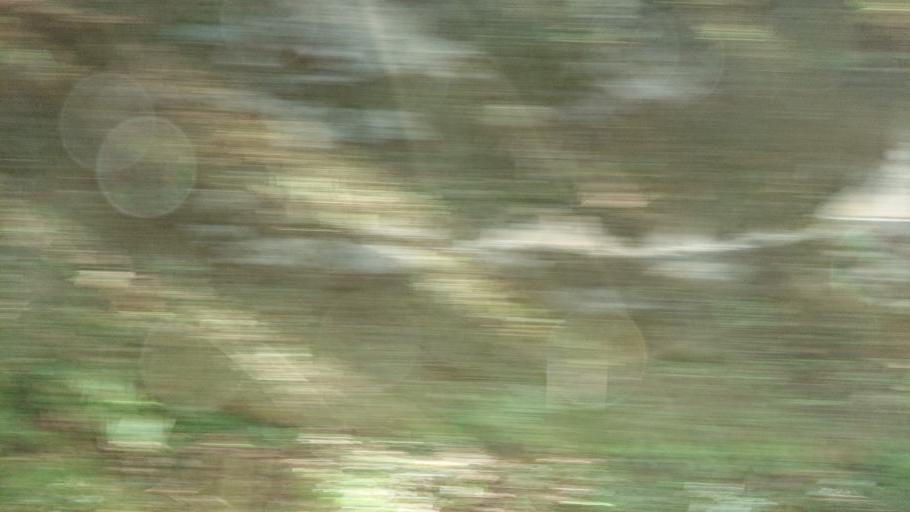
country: TW
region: Taiwan
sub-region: Hualien
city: Hualian
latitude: 24.3477
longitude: 121.3098
